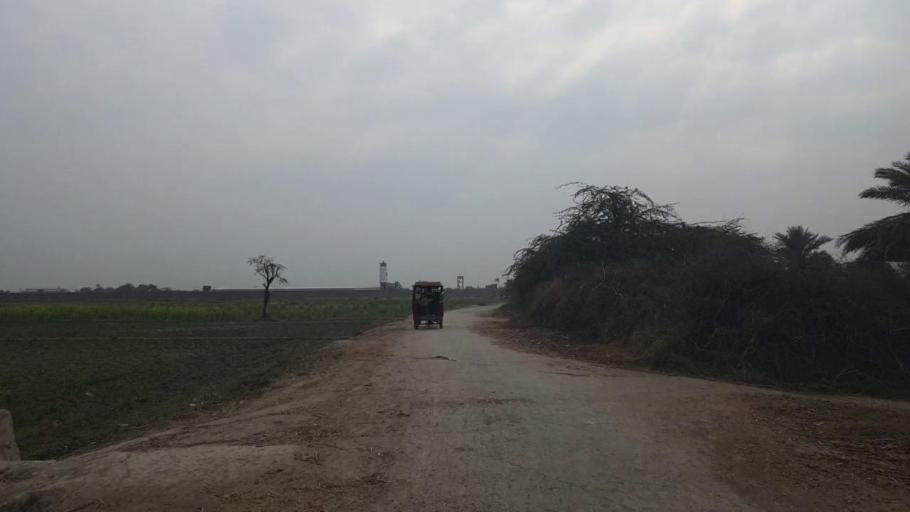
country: PK
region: Sindh
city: Shahdadpur
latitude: 25.9398
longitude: 68.7015
